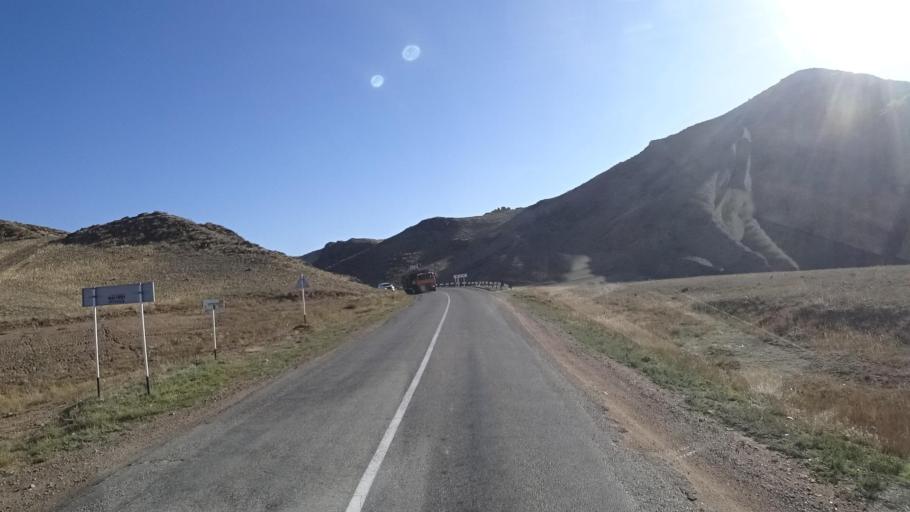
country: KZ
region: Almaty Oblysy
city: Kegen
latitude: 43.3465
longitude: 78.9281
